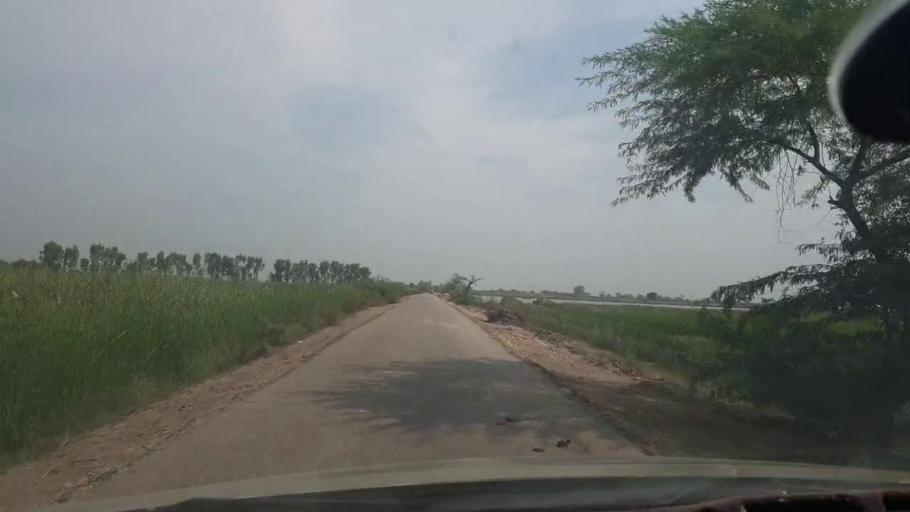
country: PK
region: Sindh
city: Jacobabad
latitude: 28.3071
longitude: 68.4755
